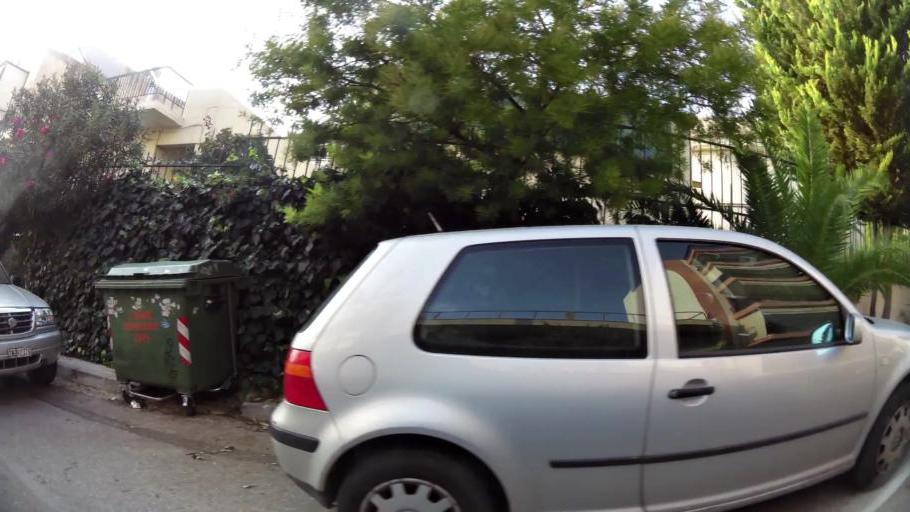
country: GR
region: Attica
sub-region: Nomarchia Athinas
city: Petroupolis
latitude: 38.0475
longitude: 23.6782
